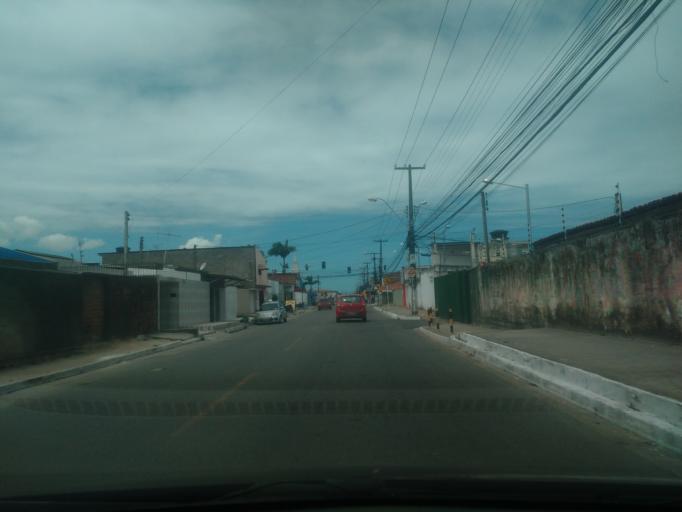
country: BR
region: Alagoas
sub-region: Satuba
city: Satuba
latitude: -9.5511
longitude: -35.7599
